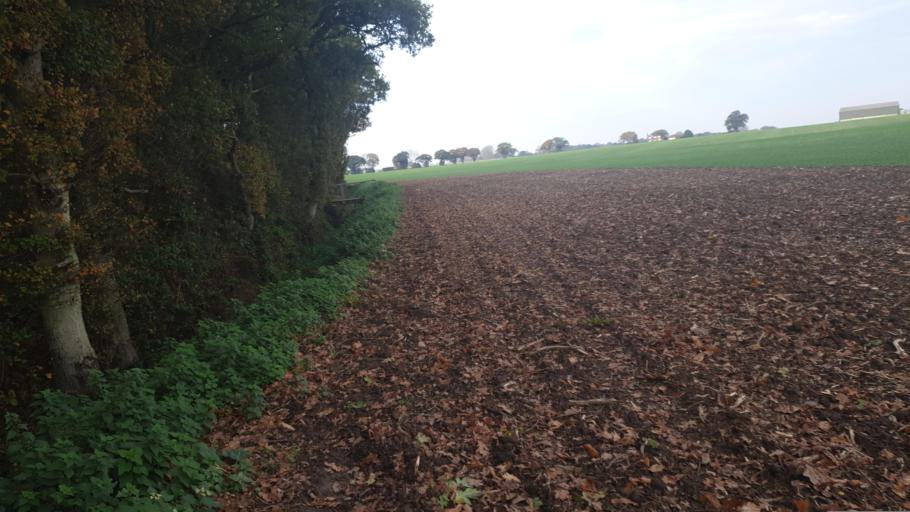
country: GB
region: England
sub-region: Essex
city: Great Bentley
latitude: 51.8868
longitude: 1.1185
